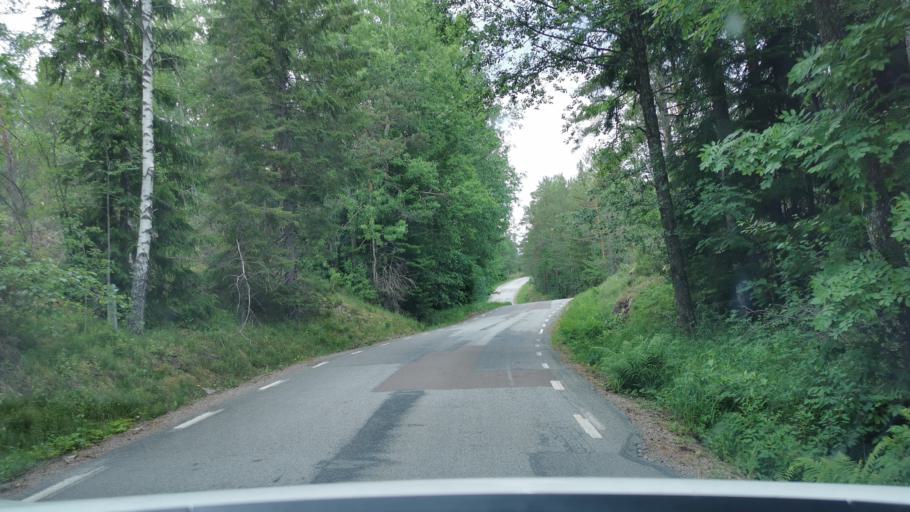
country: SE
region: Vaestra Goetaland
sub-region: Bengtsfors Kommun
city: Dals Langed
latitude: 58.8618
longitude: 12.4021
